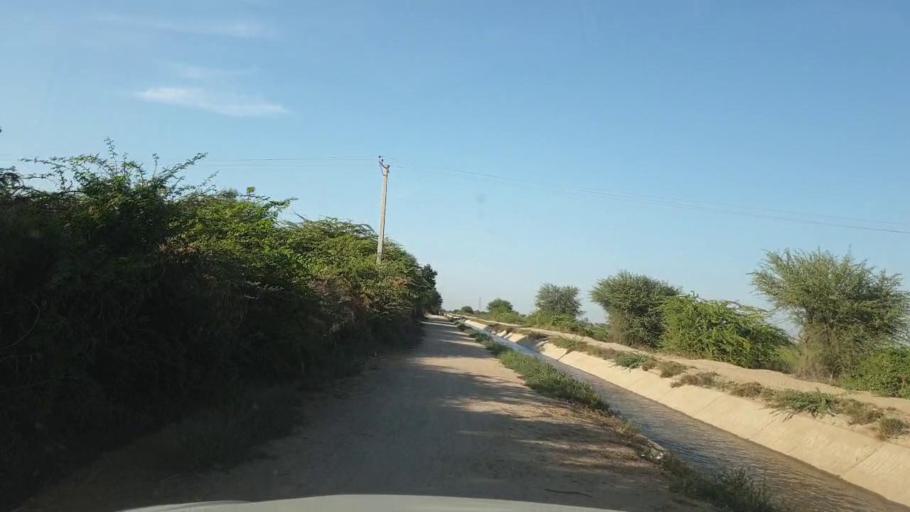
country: PK
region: Sindh
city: Kunri
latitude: 25.0950
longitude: 69.4282
